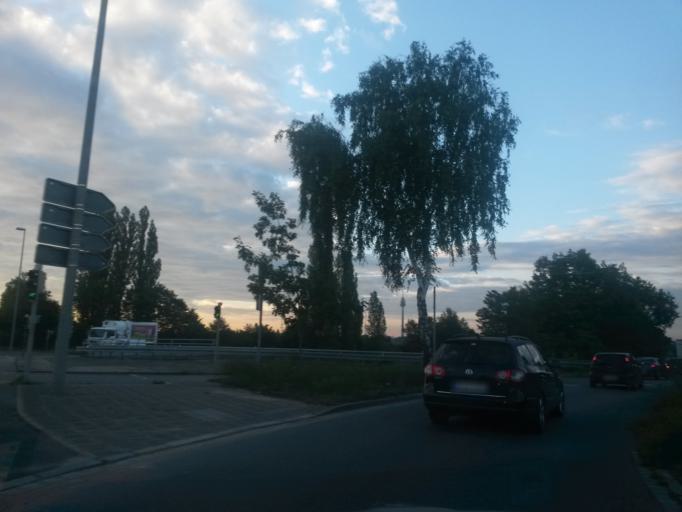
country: DE
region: Bavaria
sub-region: Regierungsbezirk Mittelfranken
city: Grossreuth bei Schweinau
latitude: 49.4384
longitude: 11.0028
